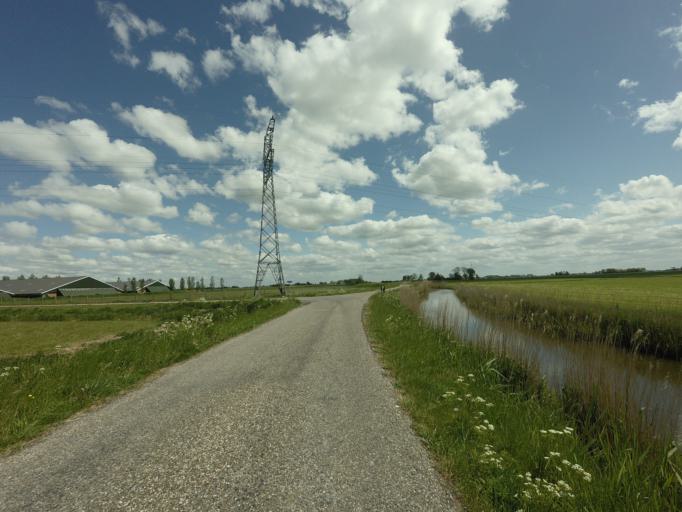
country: NL
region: Friesland
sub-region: Gemeente Franekeradeel
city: Franeker
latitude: 53.1462
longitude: 5.4993
